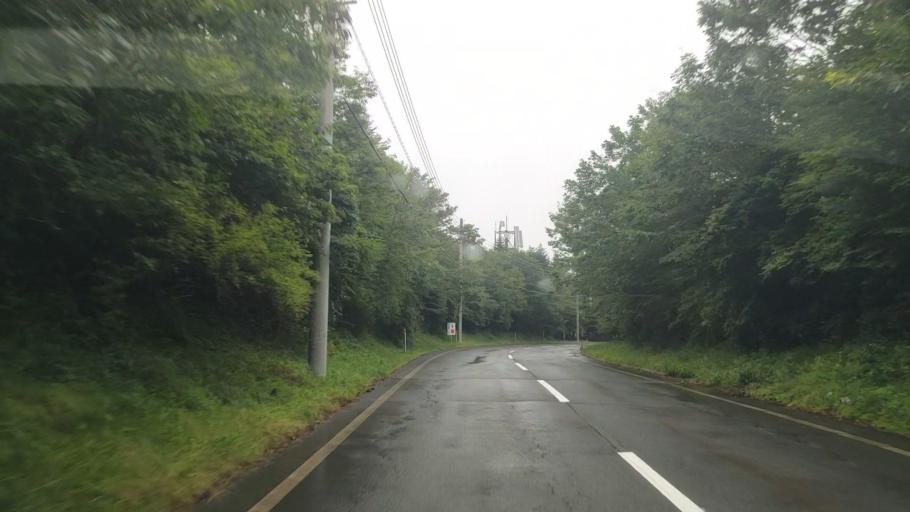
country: JP
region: Shizuoka
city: Gotemba
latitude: 35.3047
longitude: 138.7723
